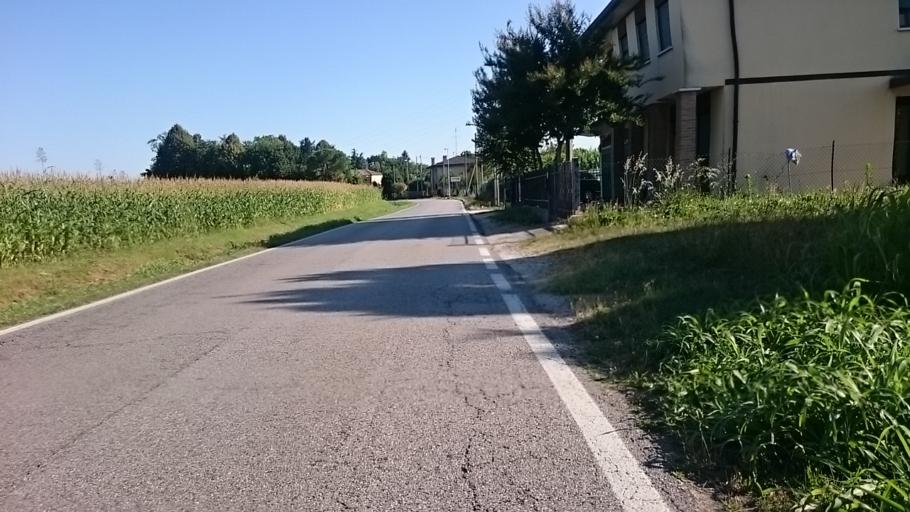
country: IT
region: Veneto
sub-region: Provincia di Padova
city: Villatora
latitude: 45.3758
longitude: 11.9691
